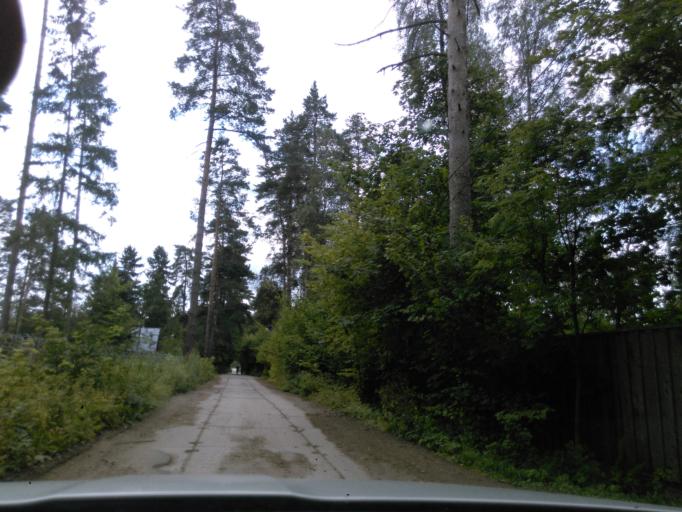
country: RU
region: Moskovskaya
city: Lozhki
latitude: 56.0518
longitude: 37.1007
